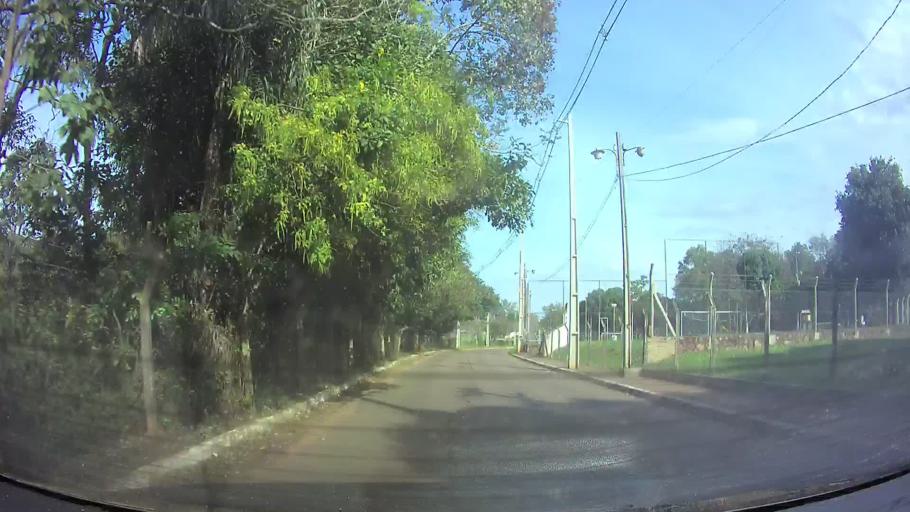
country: PY
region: Central
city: Fernando de la Mora
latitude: -25.3327
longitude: -57.5193
